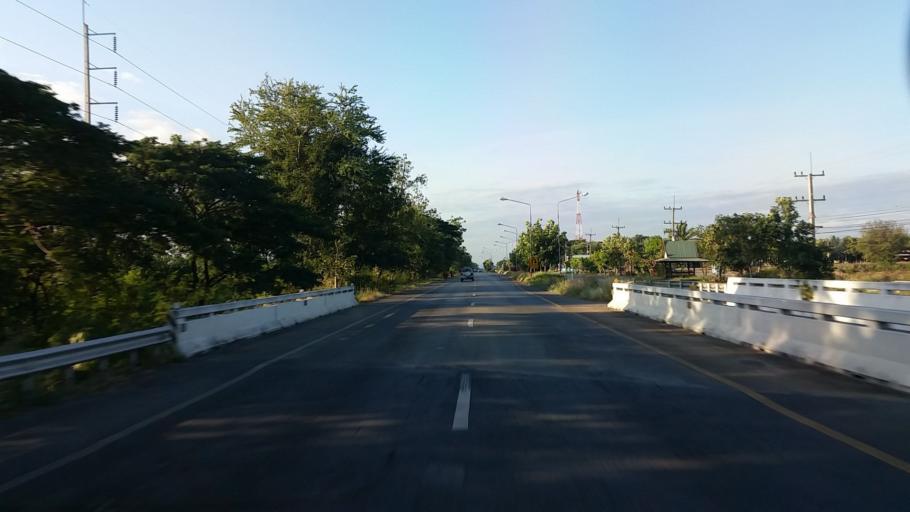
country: TH
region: Lop Buri
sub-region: Amphoe Tha Luang
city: Tha Luang
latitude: 15.1274
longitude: 101.0374
